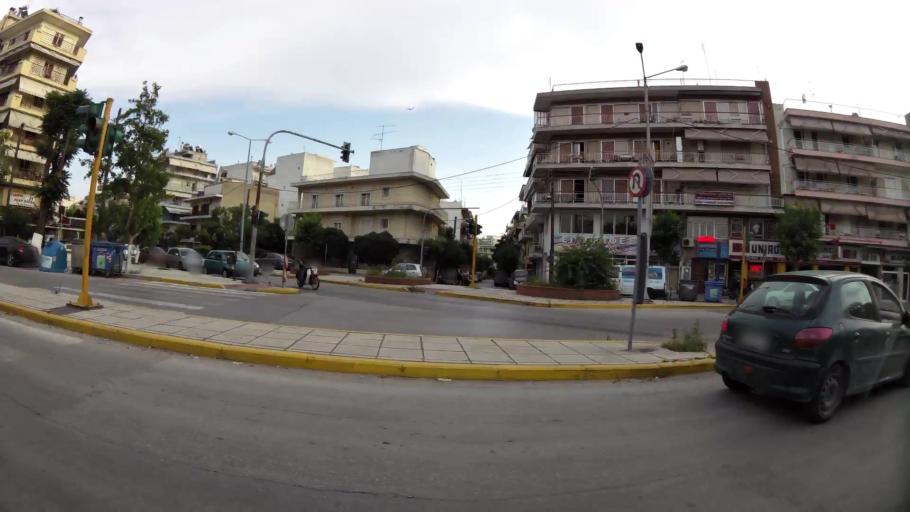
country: GR
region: Central Macedonia
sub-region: Nomos Thessalonikis
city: Ampelokipoi
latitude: 40.6579
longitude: 22.9260
